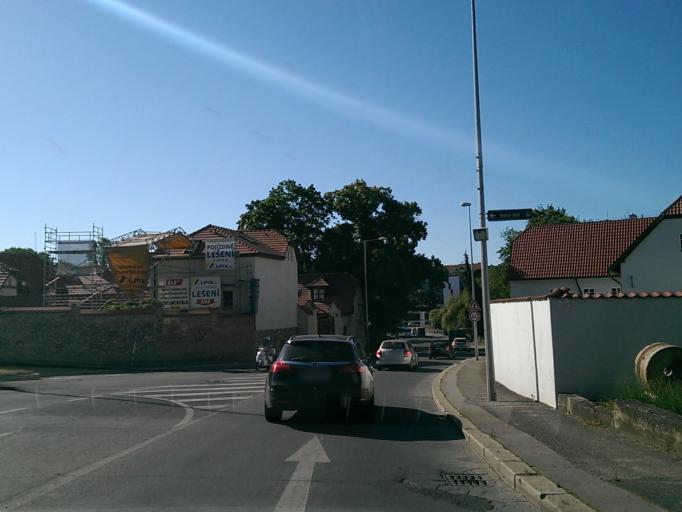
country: CZ
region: Praha
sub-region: Praha 14
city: Hostavice
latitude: 50.0492
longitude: 14.5274
